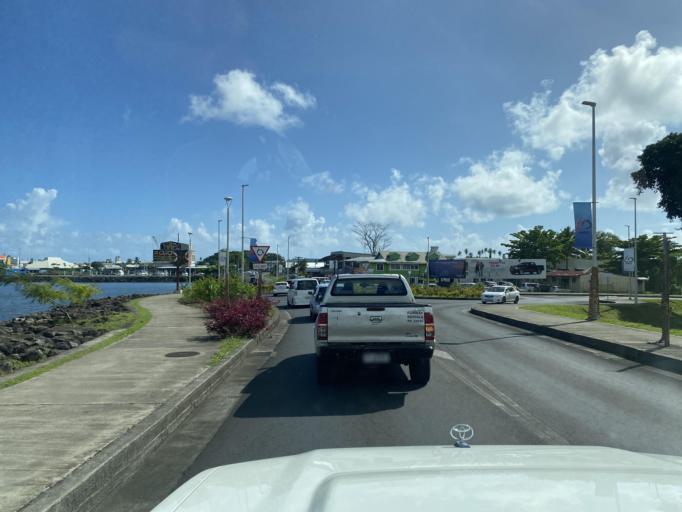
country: WS
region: Tuamasaga
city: Apia
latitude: -13.8311
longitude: -171.7602
